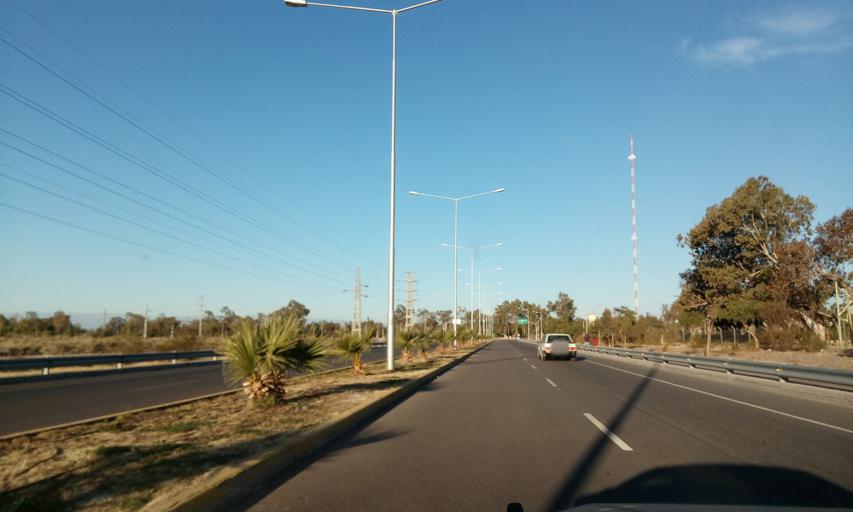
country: AR
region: San Juan
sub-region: Departamento de Rivadavia
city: Rivadavia
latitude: -31.5149
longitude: -68.6343
